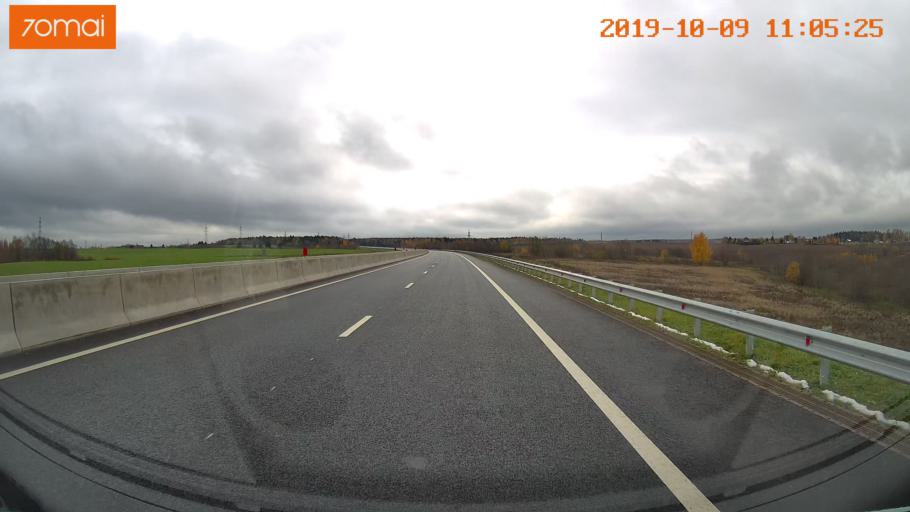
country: RU
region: Vologda
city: Molochnoye
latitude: 59.2003
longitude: 39.7591
